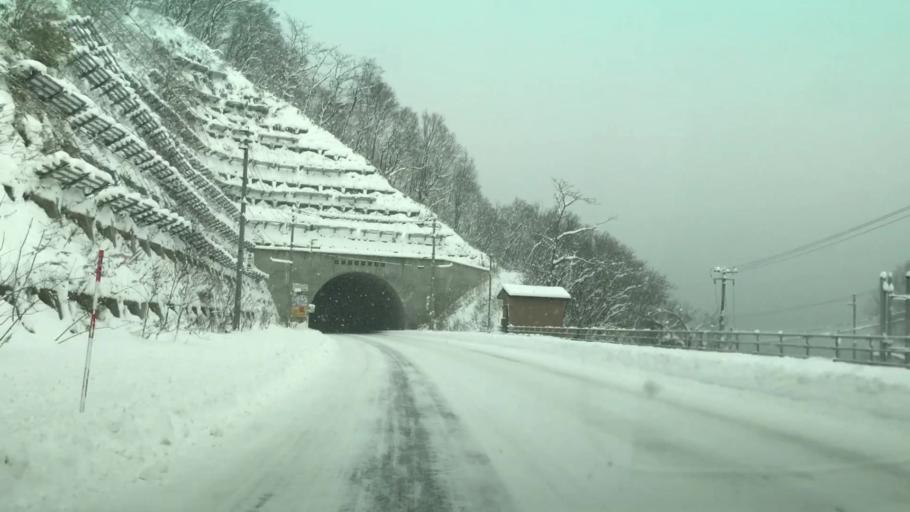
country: JP
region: Hokkaido
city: Yoichi
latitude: 43.2330
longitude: 140.7358
